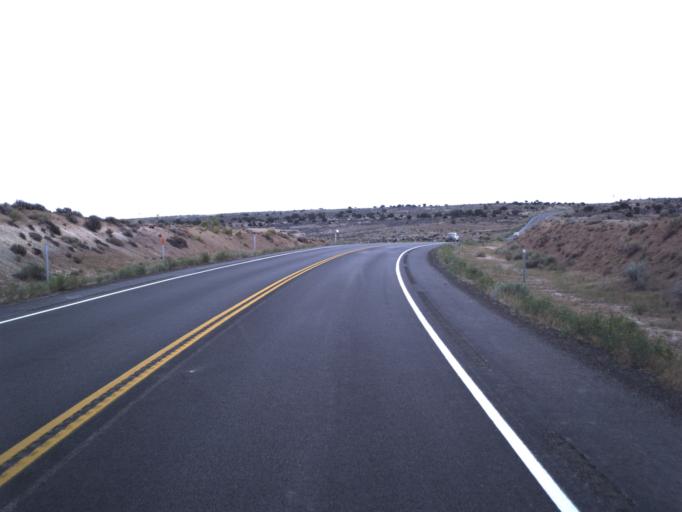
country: US
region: Utah
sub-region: Uintah County
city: Naples
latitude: 40.1981
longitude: -109.3363
